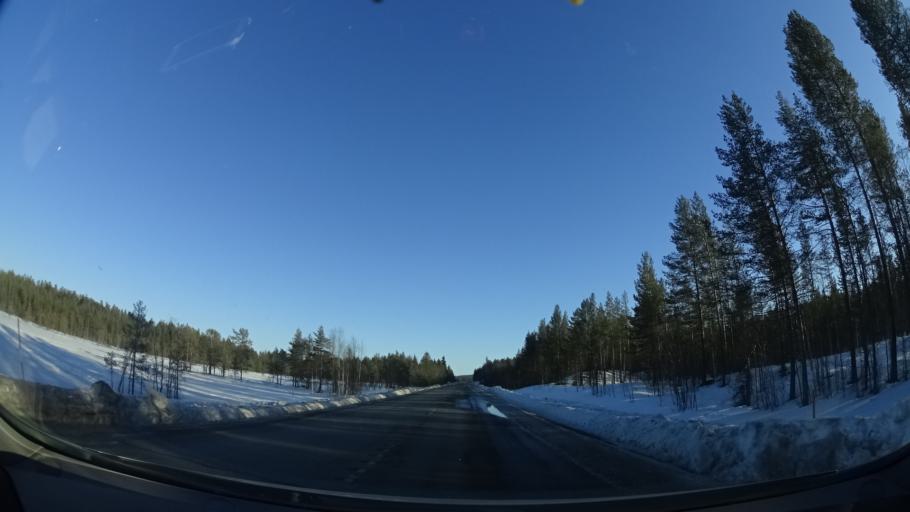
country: SE
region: Vaesterbotten
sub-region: Skelleftea Kommun
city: Langsele
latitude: 65.0491
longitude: 20.0662
